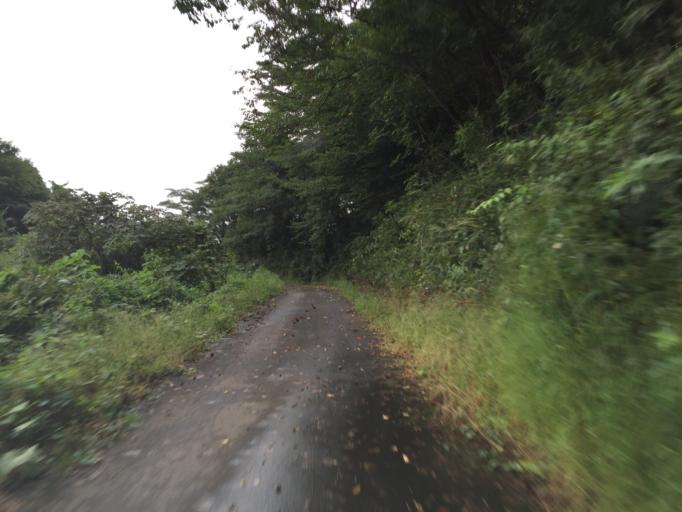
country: JP
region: Fukushima
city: Hobaramachi
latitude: 37.7634
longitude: 140.5337
